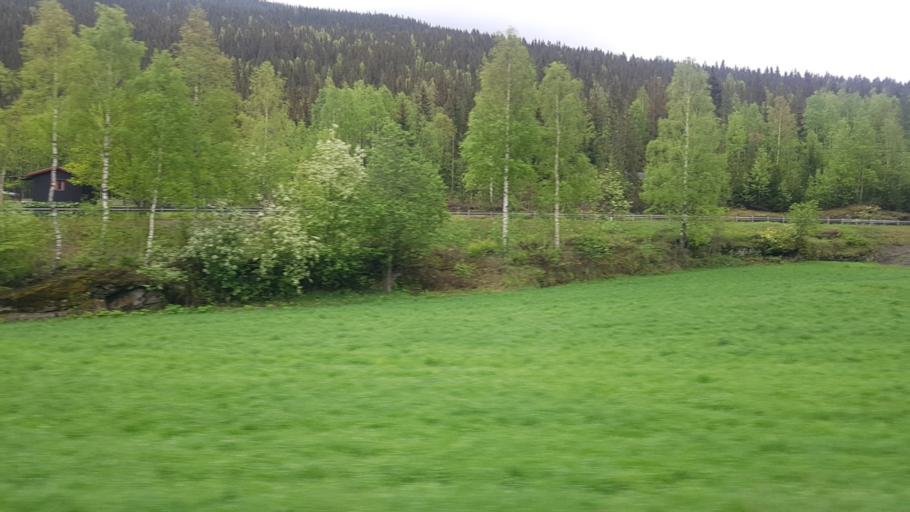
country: NO
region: Oppland
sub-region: Nord-Fron
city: Vinstra
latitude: 61.6196
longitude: 9.7122
